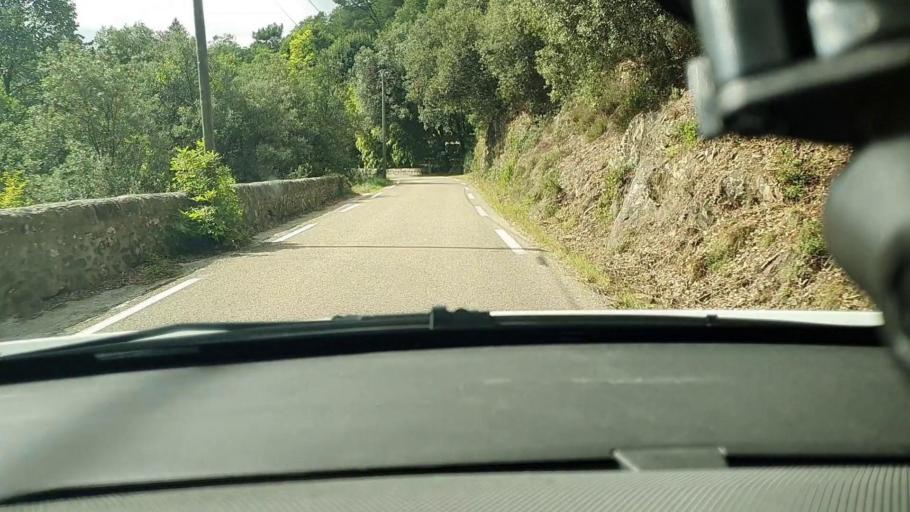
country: FR
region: Languedoc-Roussillon
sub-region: Departement du Gard
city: Branoux-les-Taillades
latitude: 44.3071
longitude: 3.9991
